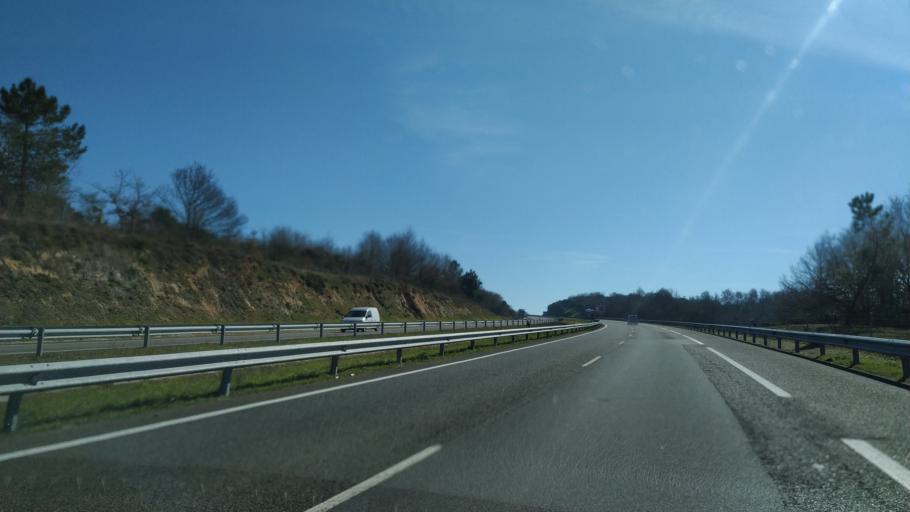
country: ES
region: Galicia
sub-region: Provincia de Ourense
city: Taboadela
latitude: 42.2183
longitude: -7.8424
